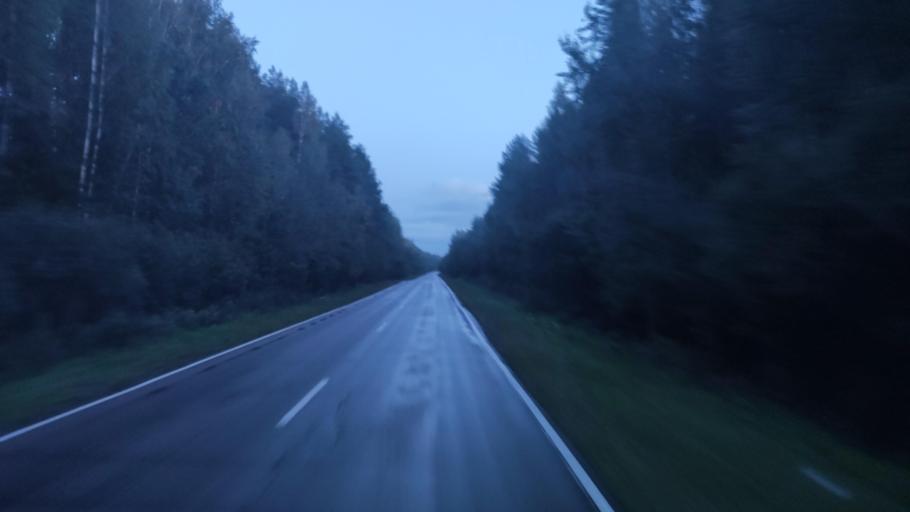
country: RU
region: Vladimir
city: Galitsy
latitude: 56.1426
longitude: 42.8673
